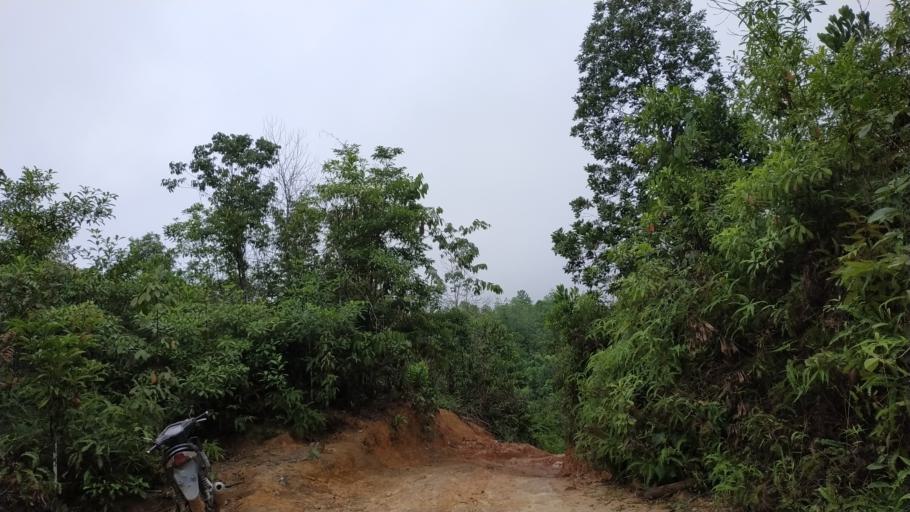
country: ID
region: Riau
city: Pekanbaru
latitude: 0.4863
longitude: 101.5653
